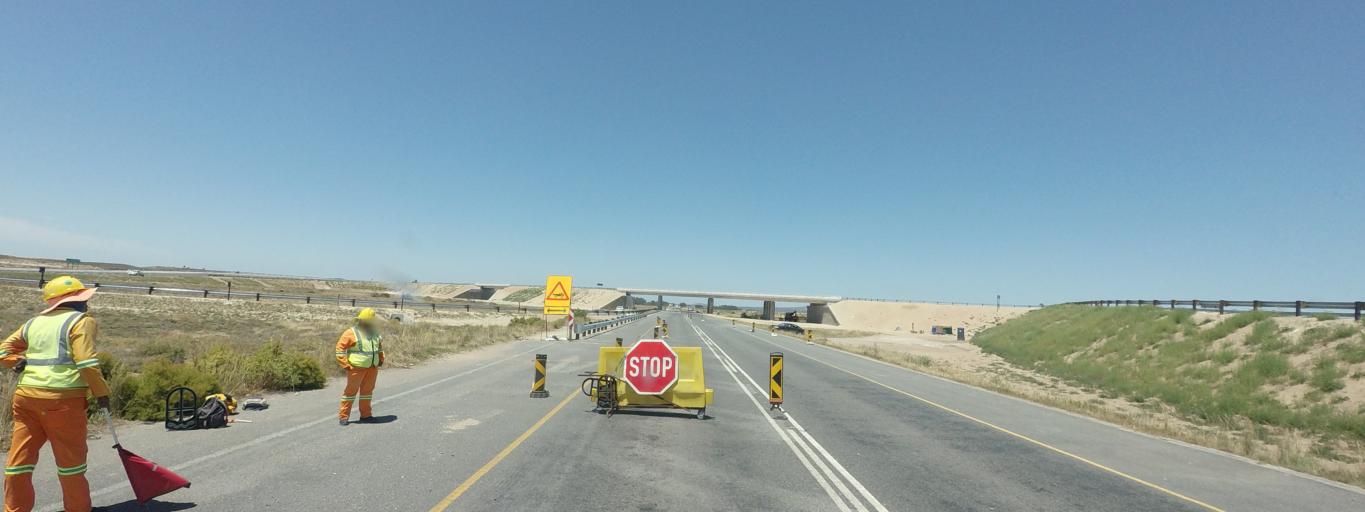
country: ZA
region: Western Cape
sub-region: West Coast District Municipality
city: Vredenburg
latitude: -32.9751
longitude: 18.0863
